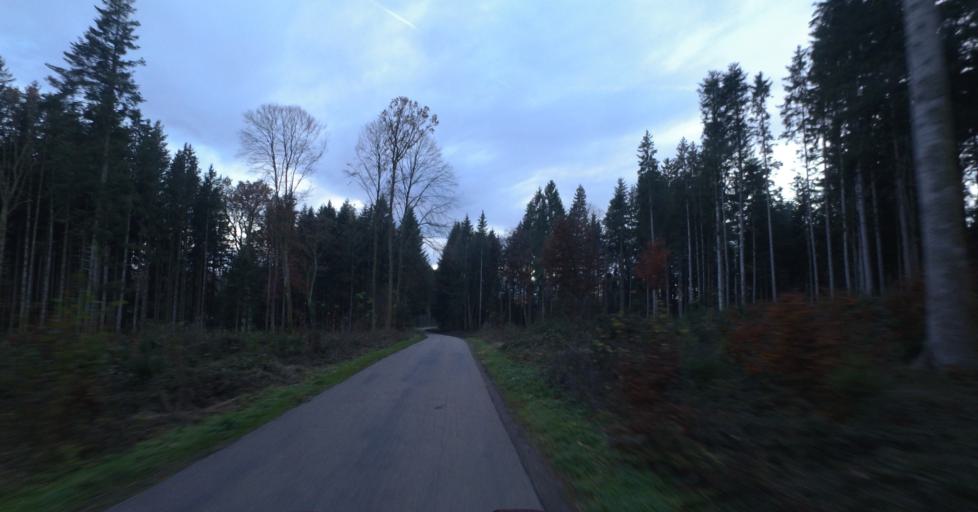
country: DE
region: Bavaria
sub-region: Upper Bavaria
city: Gstadt am Chiemsee
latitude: 47.8982
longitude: 12.4120
